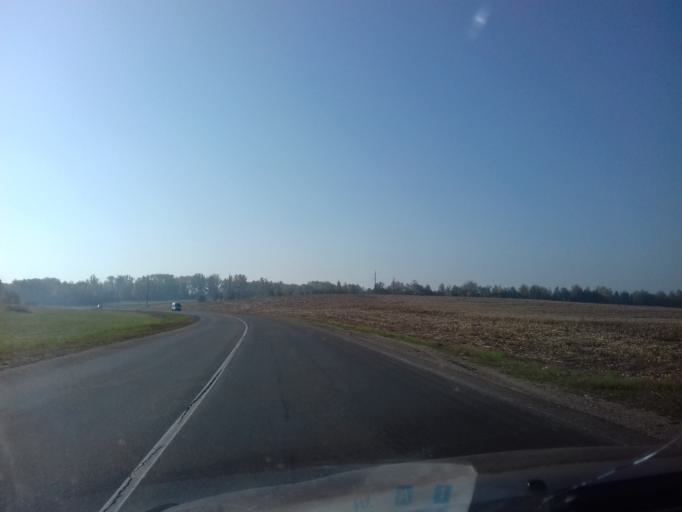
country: BY
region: Minsk
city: Hatava
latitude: 53.7724
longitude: 27.6375
